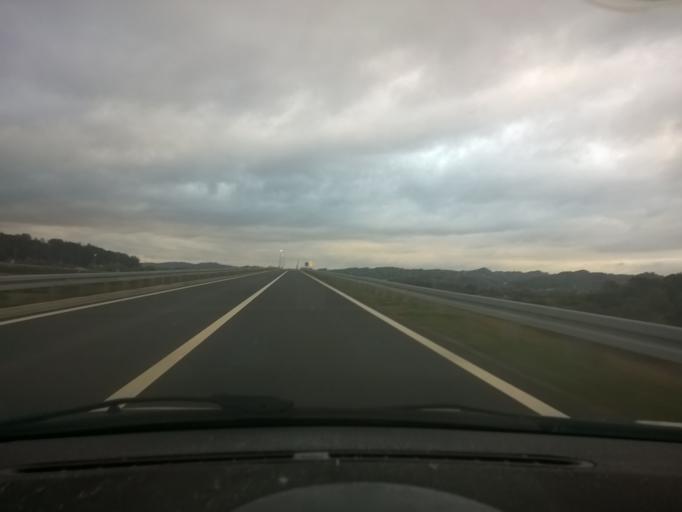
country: HR
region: Krapinsko-Zagorska
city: Zabok
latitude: 46.0142
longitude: 15.9268
